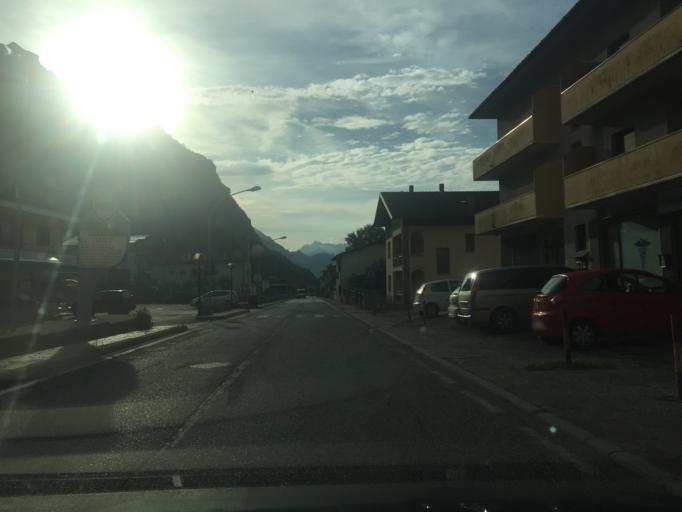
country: IT
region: Friuli Venezia Giulia
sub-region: Provincia di Udine
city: Villa Santina
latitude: 46.4179
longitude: 12.9156
